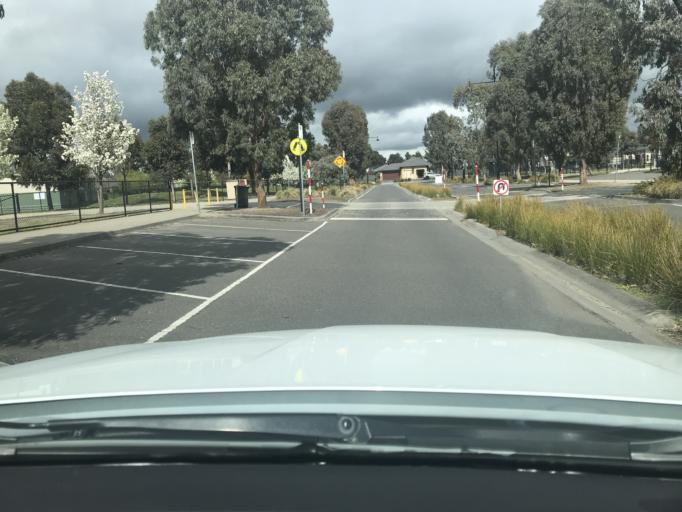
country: AU
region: Victoria
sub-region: Hume
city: Craigieburn
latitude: -37.5792
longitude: 144.9239
